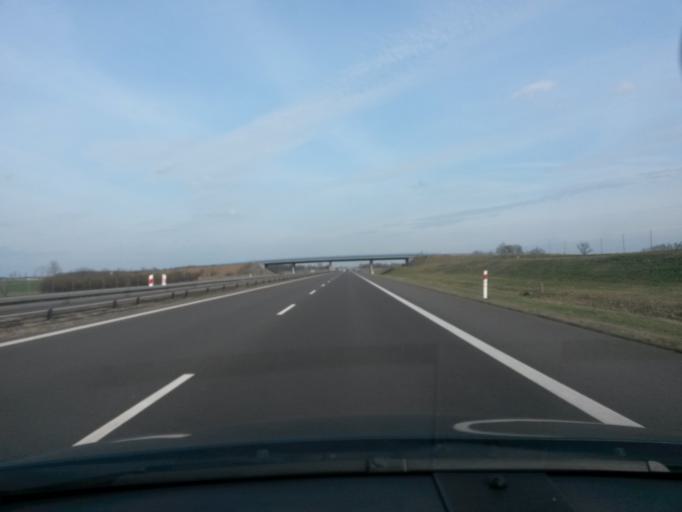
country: PL
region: Greater Poland Voivodeship
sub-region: Powiat wrzesinski
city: Nekla
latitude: 52.3186
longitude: 17.4640
